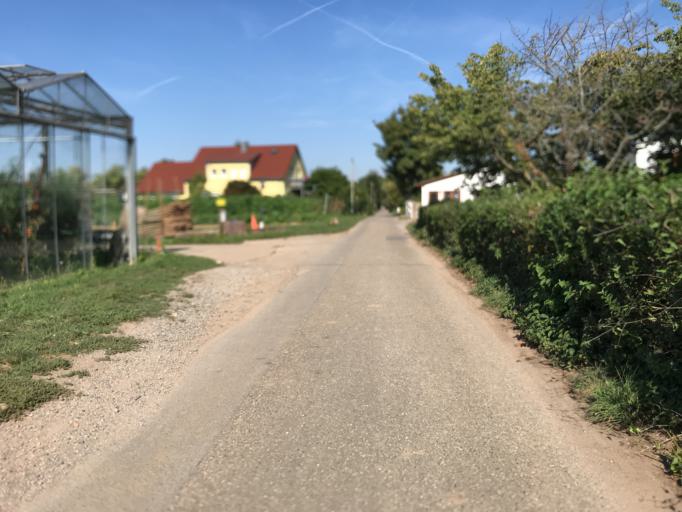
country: DE
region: Baden-Wuerttemberg
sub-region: Karlsruhe Region
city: Heidelberg
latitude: 49.4242
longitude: 8.6780
